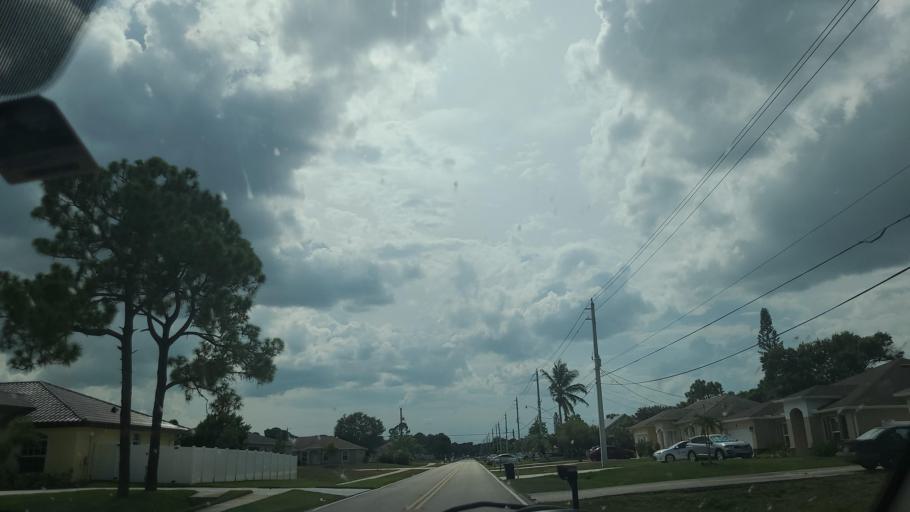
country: US
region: Florida
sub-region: Saint Lucie County
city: Port Saint Lucie
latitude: 27.2425
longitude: -80.3686
